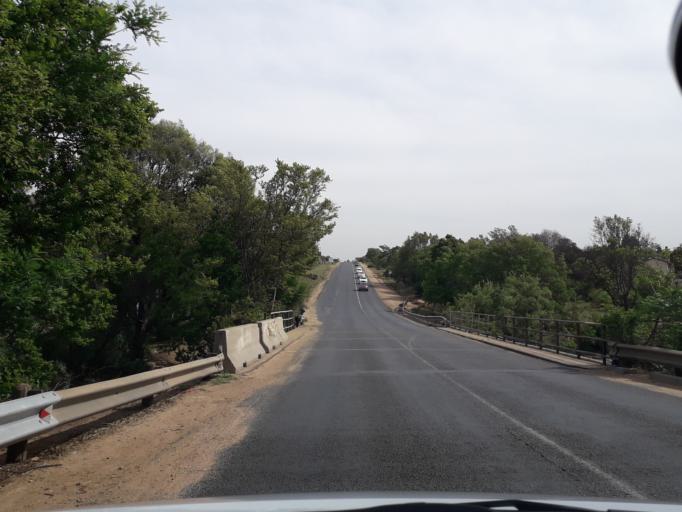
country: ZA
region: Gauteng
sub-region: City of Johannesburg Metropolitan Municipality
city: Diepsloot
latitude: -26.0092
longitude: 28.0380
